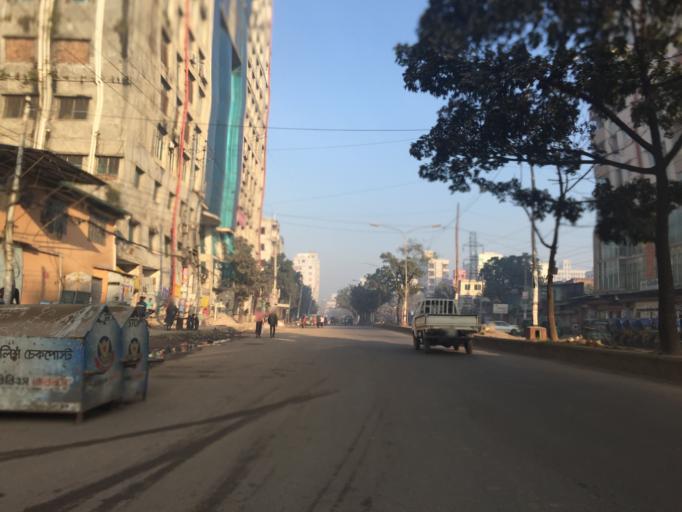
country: BD
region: Dhaka
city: Azimpur
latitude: 23.8026
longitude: 90.3534
